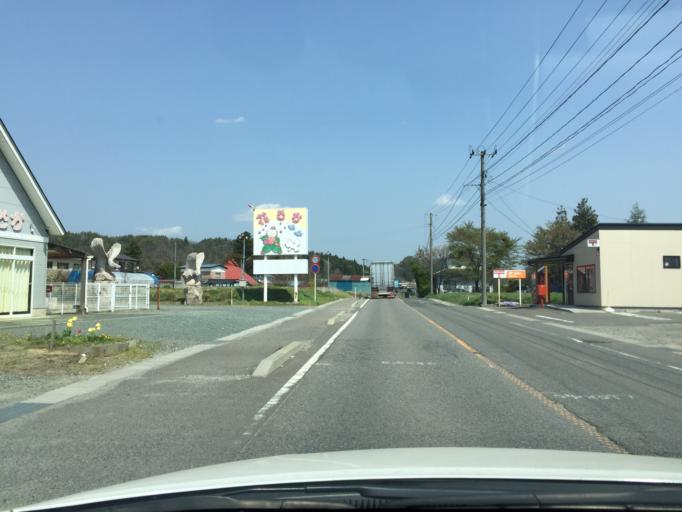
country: JP
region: Fukushima
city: Funehikimachi-funehiki
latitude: 37.4419
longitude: 140.6069
